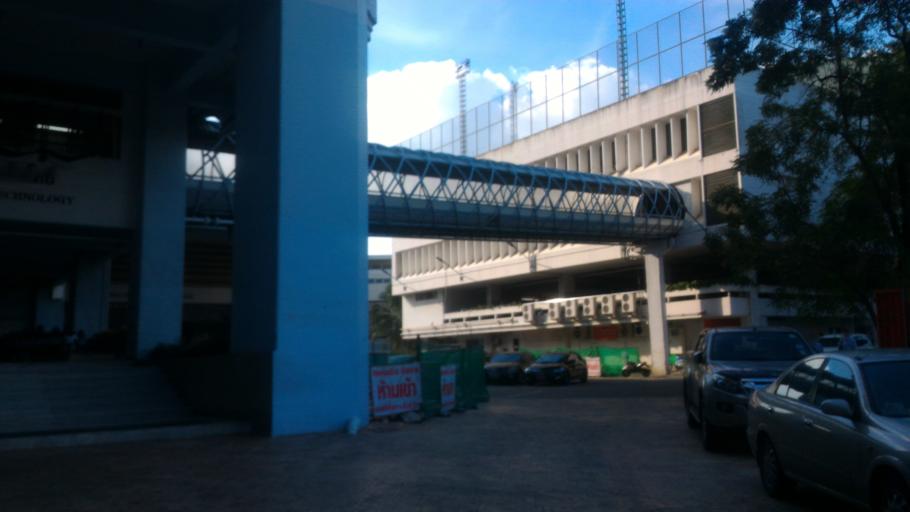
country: TH
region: Bangkok
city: Thung Khru
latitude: 13.6502
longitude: 100.4922
